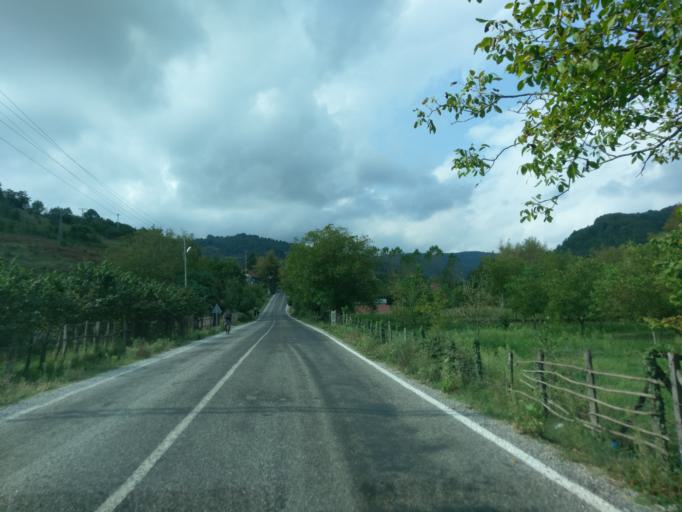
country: TR
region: Sinop
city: Helaldi
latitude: 41.9235
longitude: 34.4145
